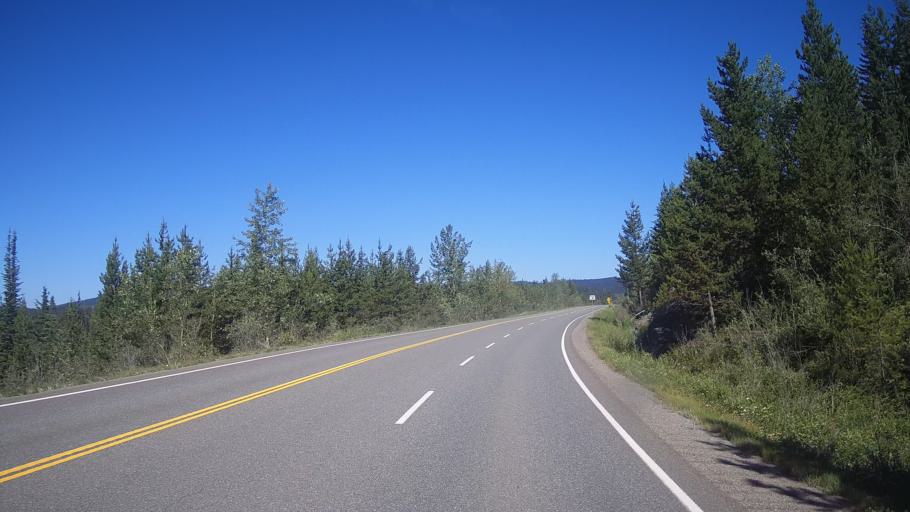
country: CA
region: British Columbia
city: Kamloops
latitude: 51.4950
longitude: -120.3361
